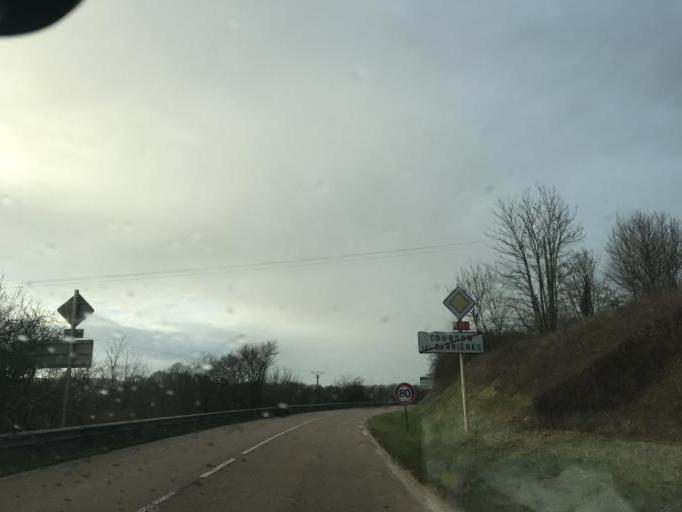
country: FR
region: Bourgogne
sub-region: Departement de l'Yonne
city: Fontenailles
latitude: 47.6153
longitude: 3.4972
